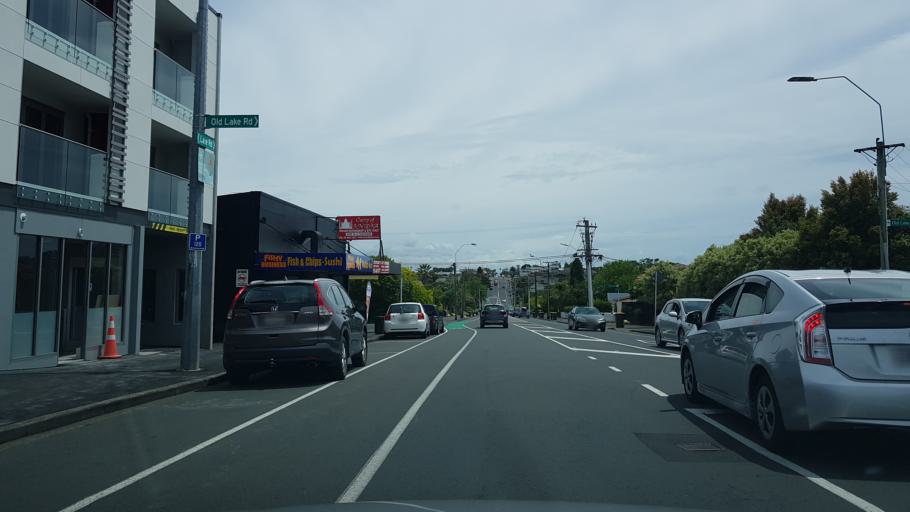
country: NZ
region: Auckland
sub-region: Auckland
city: North Shore
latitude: -36.8130
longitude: 174.7924
